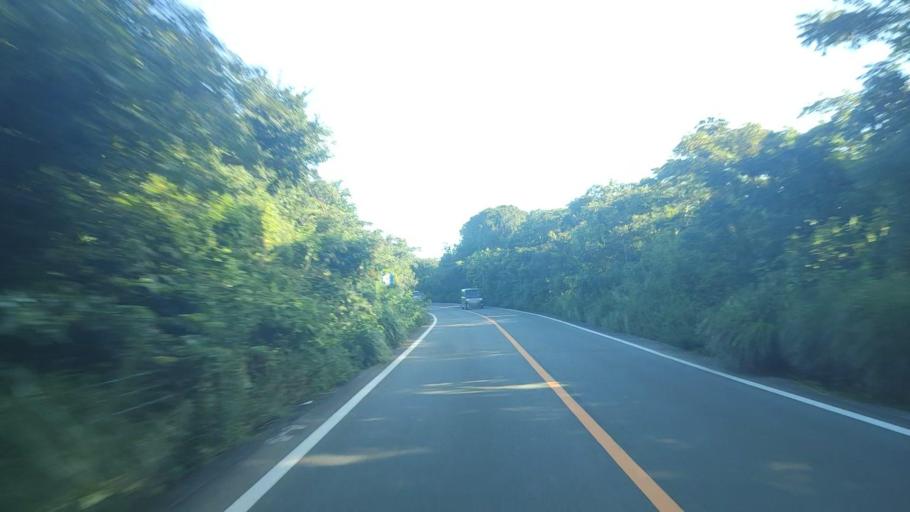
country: JP
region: Mie
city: Toba
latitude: 34.3382
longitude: 136.8394
